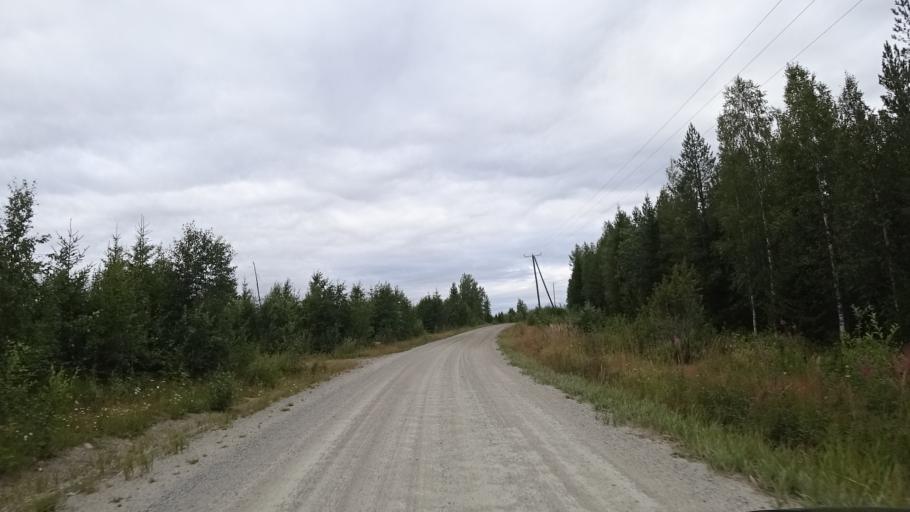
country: FI
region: North Karelia
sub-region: Joensuu
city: Eno
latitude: 63.1610
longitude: 30.5797
